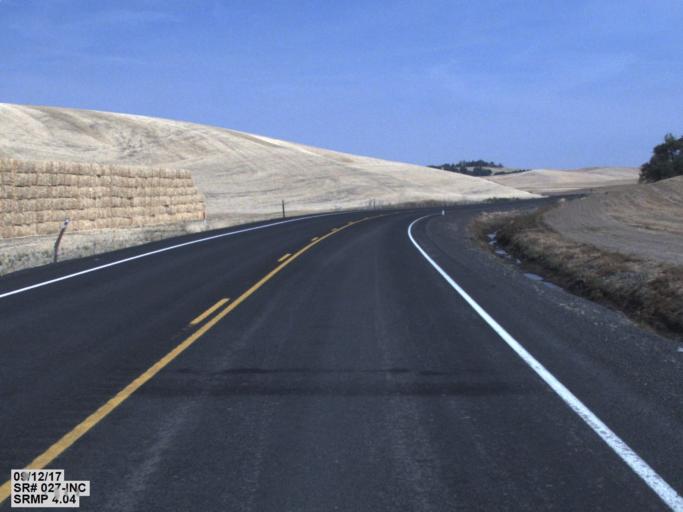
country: US
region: Washington
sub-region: Whitman County
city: Pullman
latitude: 46.7827
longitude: -117.1503
